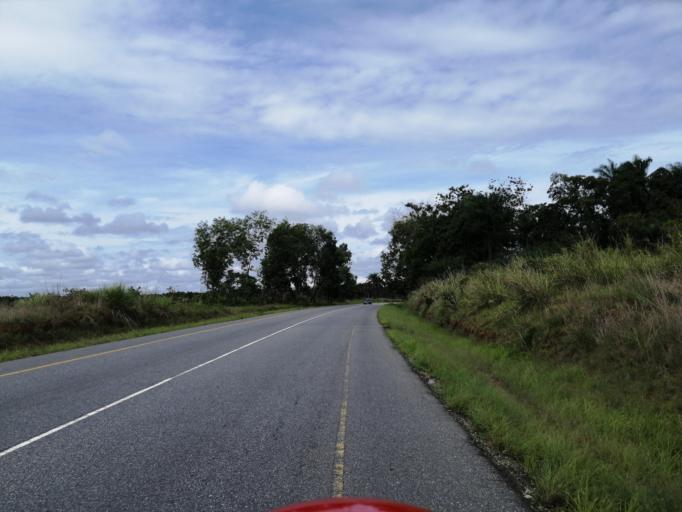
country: SL
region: Northern Province
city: Port Loko
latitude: 8.7299
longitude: -12.9506
